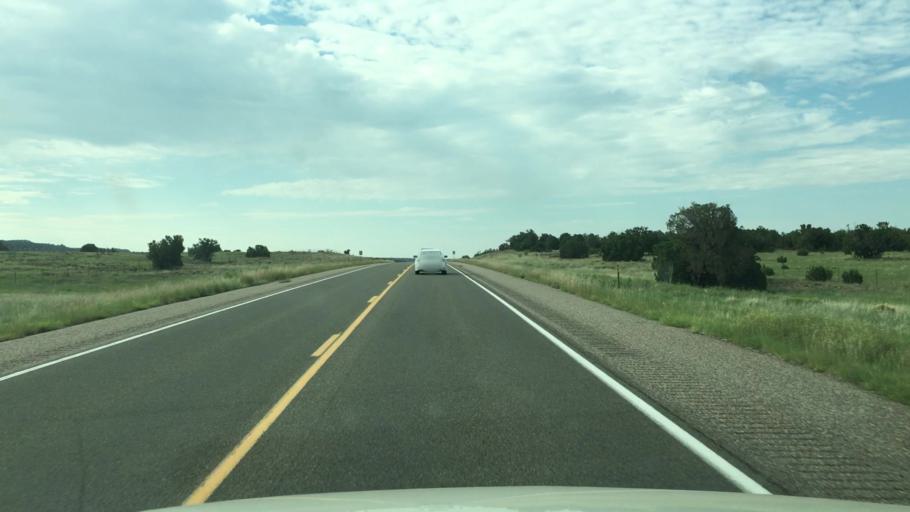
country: US
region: New Mexico
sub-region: Santa Fe County
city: Eldorado at Santa Fe
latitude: 35.3140
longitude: -105.8304
